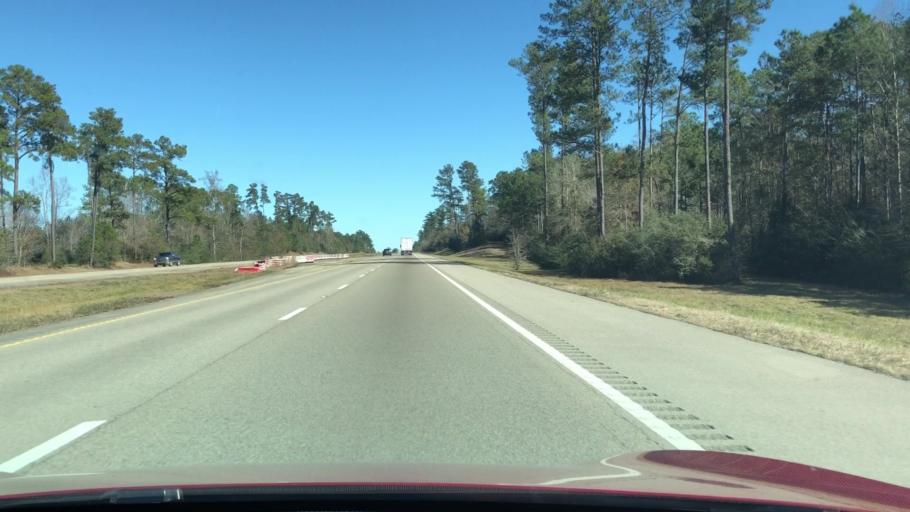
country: US
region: Mississippi
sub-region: Pearl River County
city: Poplarville
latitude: 30.7374
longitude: -89.5373
